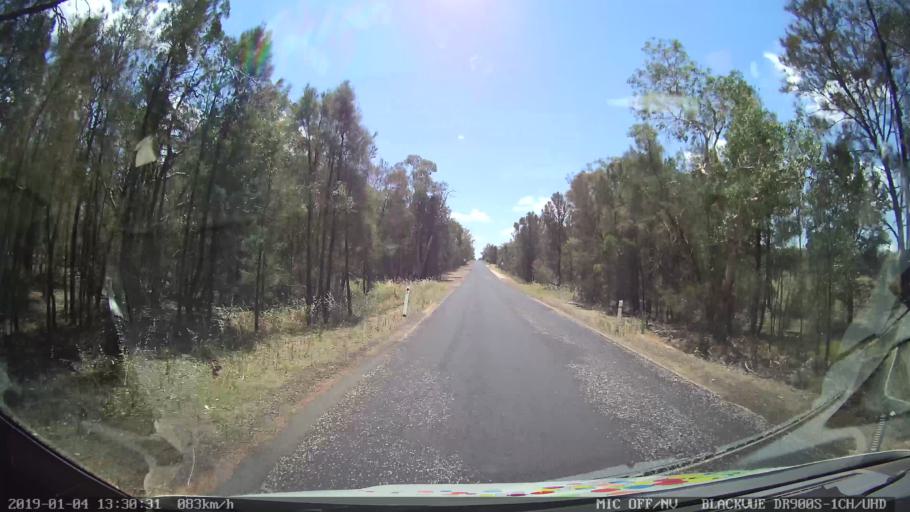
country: AU
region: New South Wales
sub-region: Parkes
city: Peak Hill
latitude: -32.6341
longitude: 148.5494
